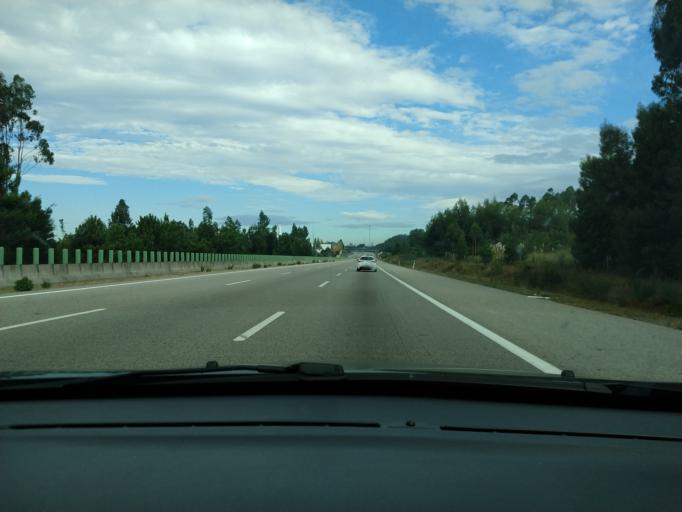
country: PT
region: Aveiro
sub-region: Ovar
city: Valega
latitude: 40.8709
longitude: -8.5599
